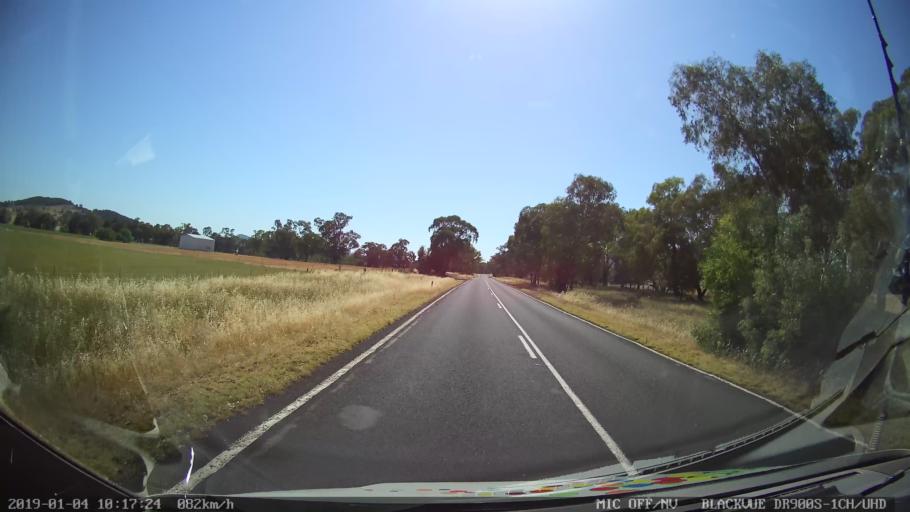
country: AU
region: New South Wales
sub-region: Cabonne
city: Canowindra
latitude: -33.3840
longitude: 148.4510
